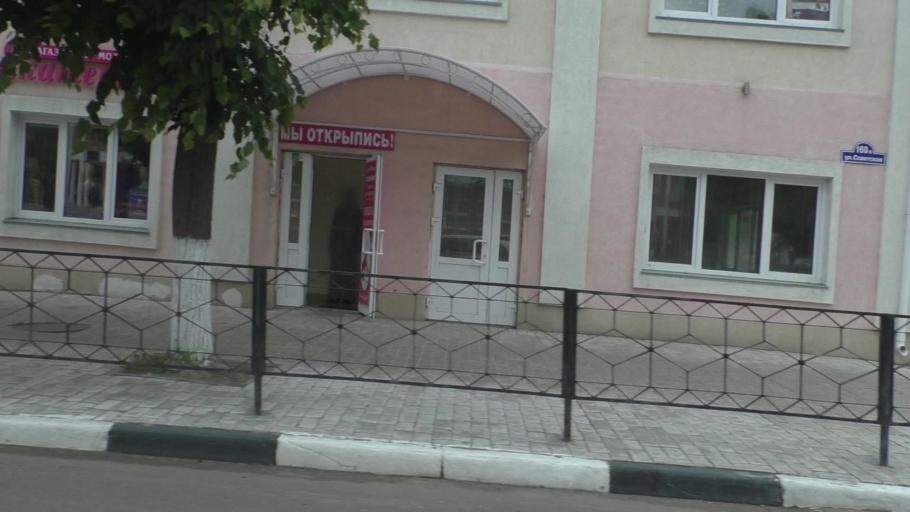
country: RU
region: Moskovskaya
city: Yegor'yevsk
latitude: 55.3776
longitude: 39.0441
